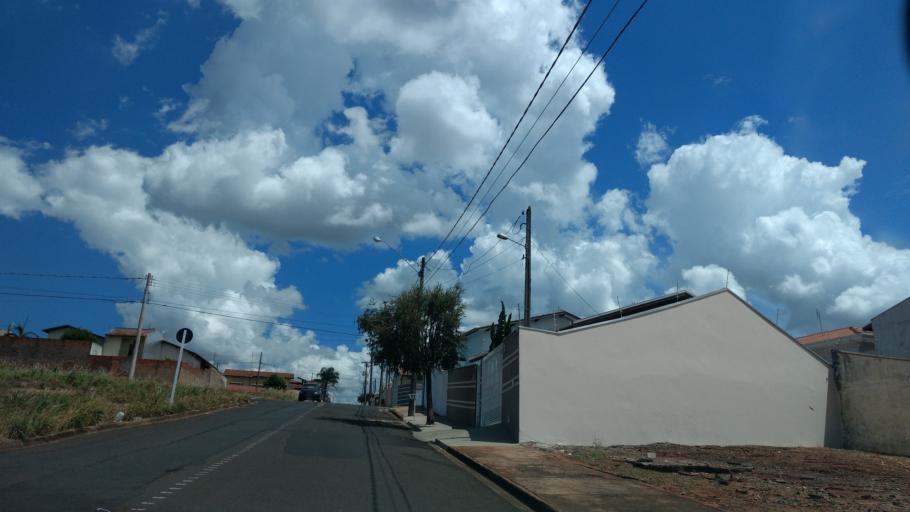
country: BR
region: Sao Paulo
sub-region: Botucatu
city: Botucatu
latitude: -22.8637
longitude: -48.4545
